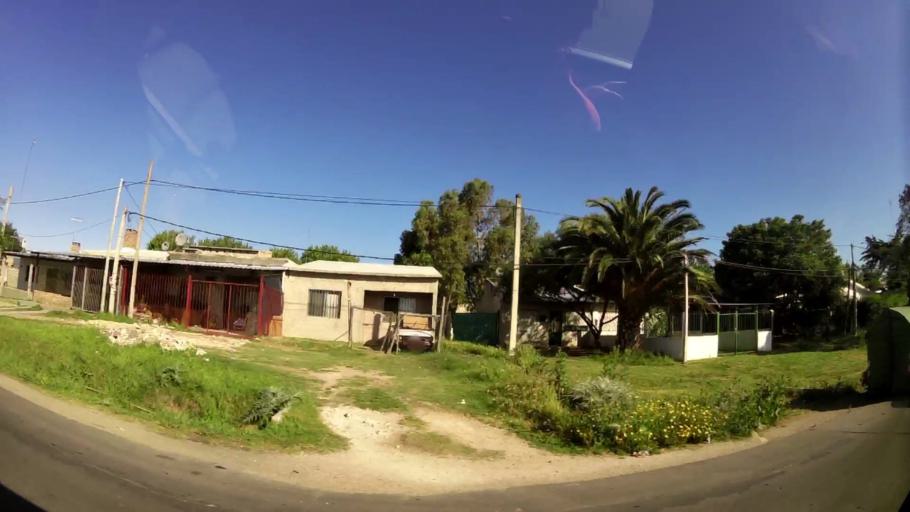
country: UY
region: Canelones
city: La Paz
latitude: -34.8223
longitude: -56.1782
